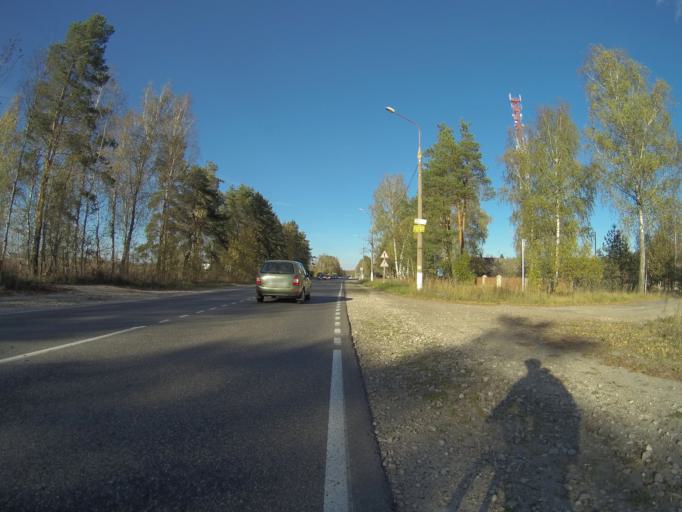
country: RU
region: Vladimir
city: Golovino
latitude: 55.9971
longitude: 40.5628
